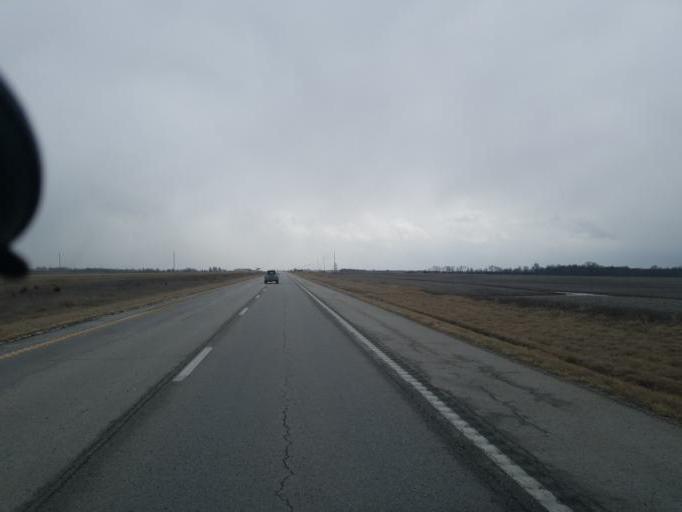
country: US
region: Missouri
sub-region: Randolph County
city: Moberly
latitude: 39.5596
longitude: -92.4590
